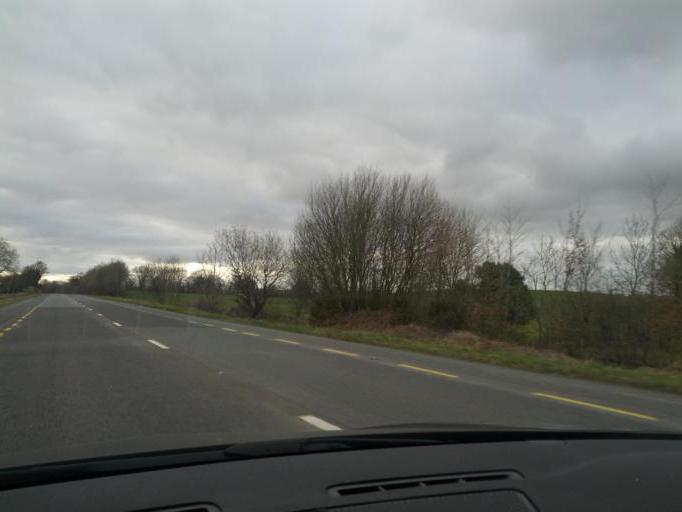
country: IE
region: Leinster
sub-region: An Iarmhi
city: Moate
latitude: 53.3907
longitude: -7.7875
